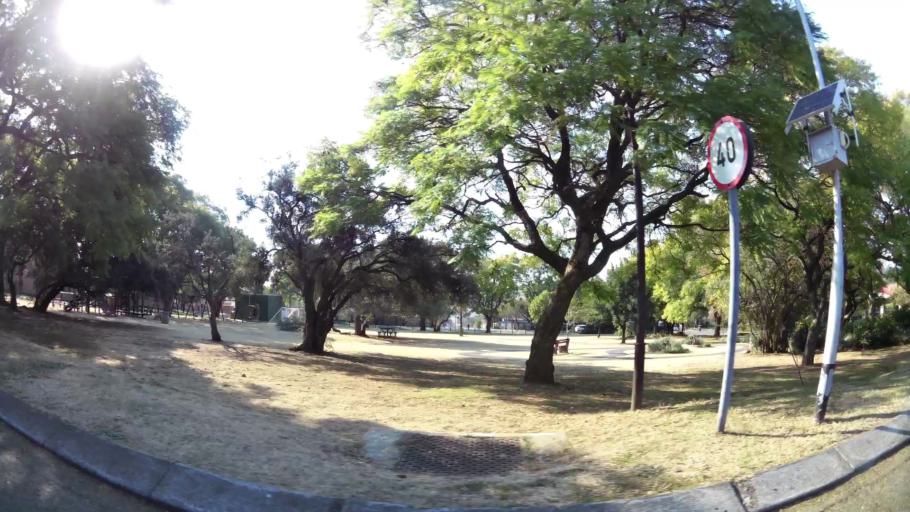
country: ZA
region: Gauteng
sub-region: City of Johannesburg Metropolitan Municipality
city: Modderfontein
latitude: -26.0991
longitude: 28.1483
